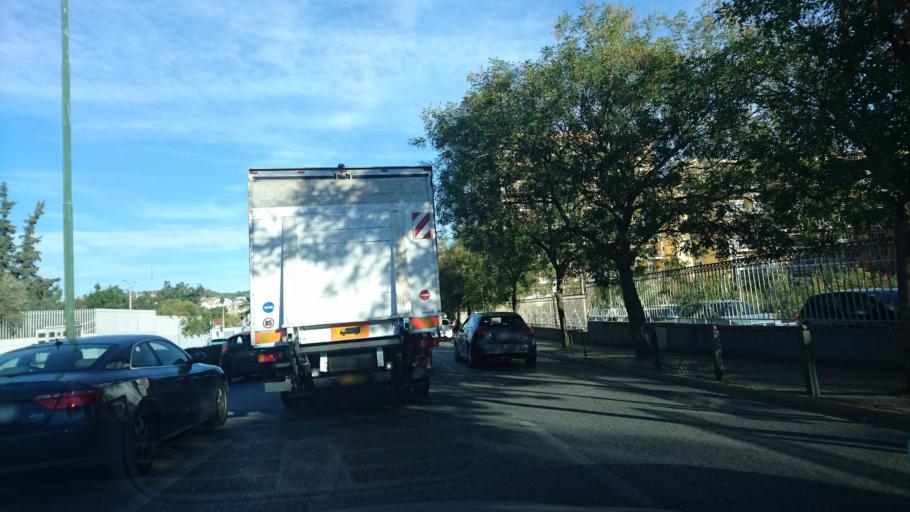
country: GR
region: Attica
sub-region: Nomarchia Athinas
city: Papagou
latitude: 37.9901
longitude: 23.7779
